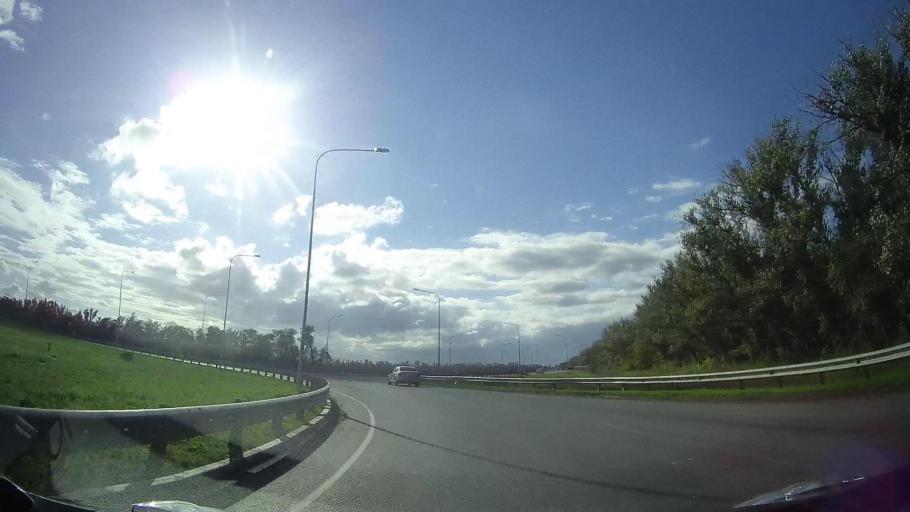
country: RU
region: Rostov
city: Tselina
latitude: 46.5332
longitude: 40.9835
